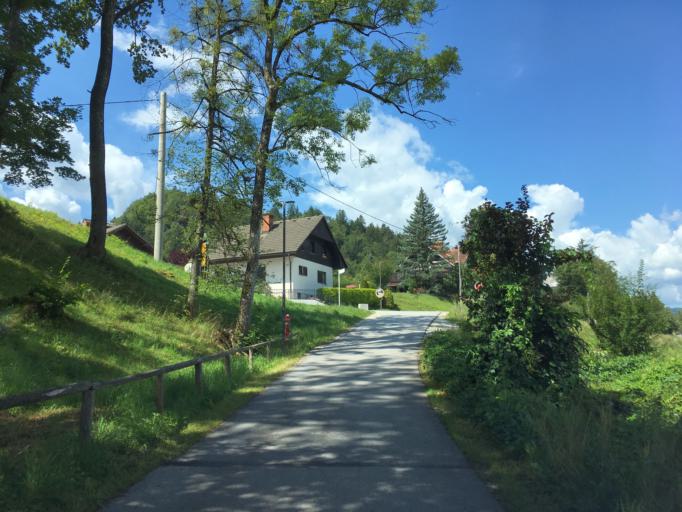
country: SI
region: Bled
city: Bled
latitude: 46.3621
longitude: 14.1147
